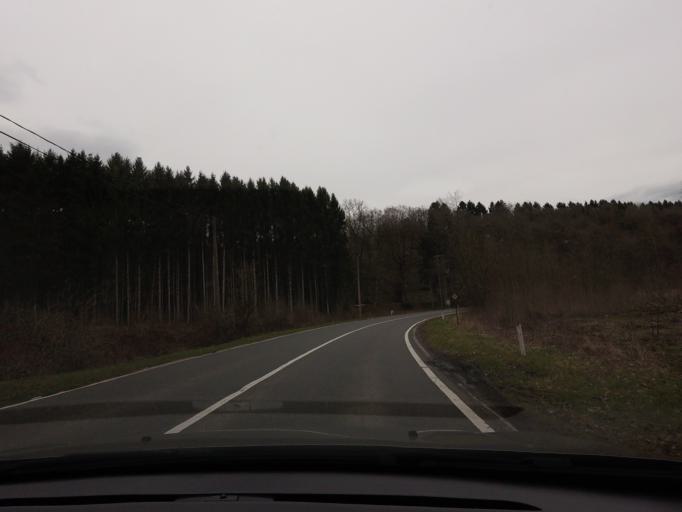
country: BE
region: Wallonia
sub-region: Province de Liege
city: Aywaille
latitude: 50.4531
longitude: 5.6681
